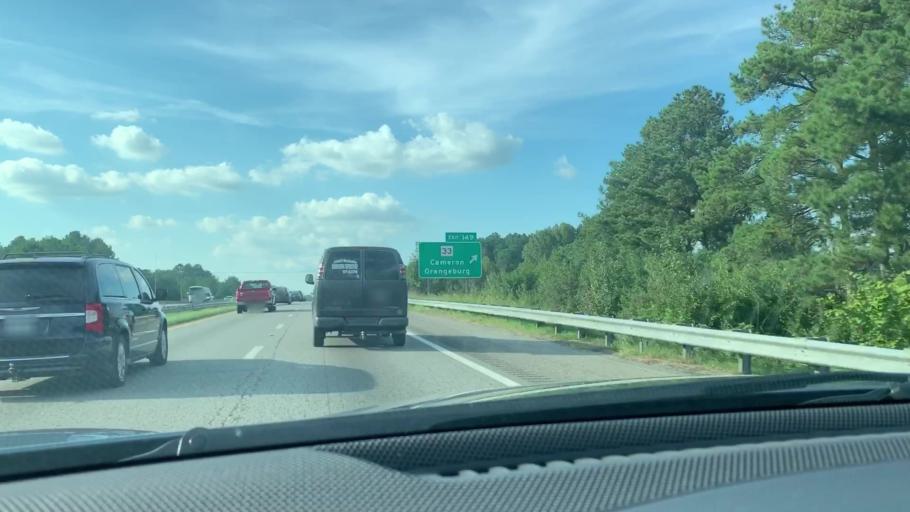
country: US
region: South Carolina
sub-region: Orangeburg County
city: Brookdale
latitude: 33.5184
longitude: -80.7895
